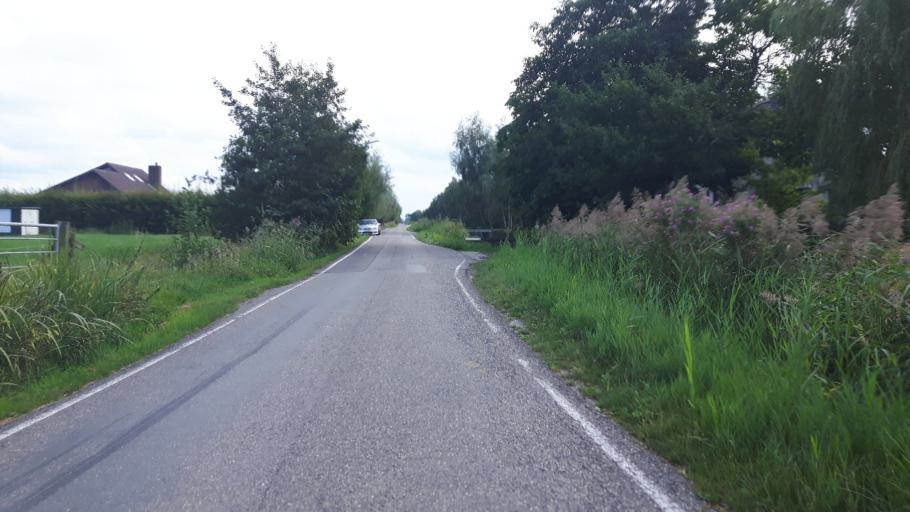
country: NL
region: Utrecht
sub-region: Gemeente De Ronde Venen
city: Mijdrecht
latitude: 52.1561
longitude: 4.8926
